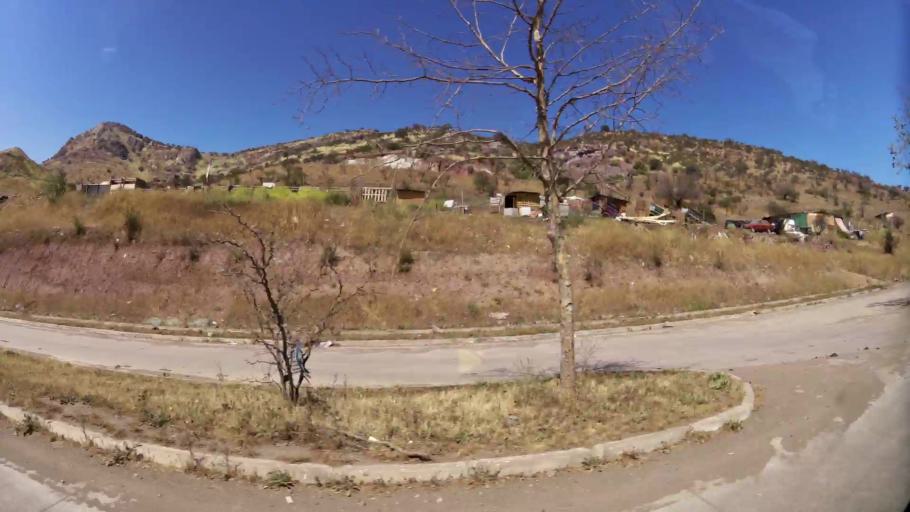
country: CL
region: Santiago Metropolitan
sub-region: Provincia de Santiago
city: Lo Prado
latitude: -33.3862
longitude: -70.7464
